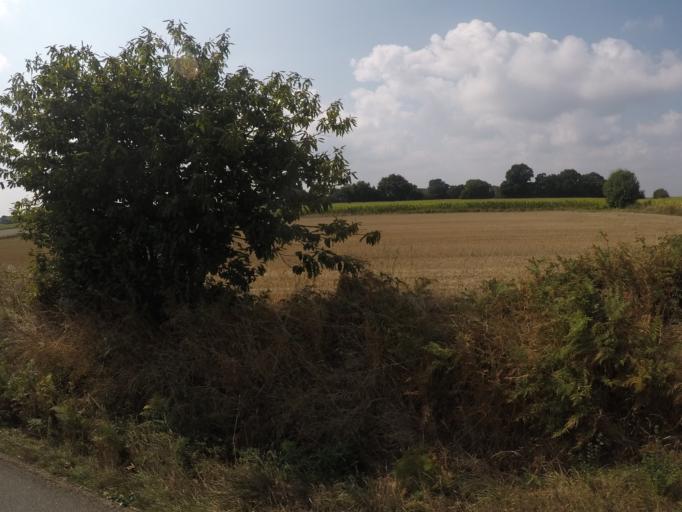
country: FR
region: Brittany
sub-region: Departement des Cotes-d'Armor
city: Tremuson
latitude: 48.5345
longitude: -2.8927
